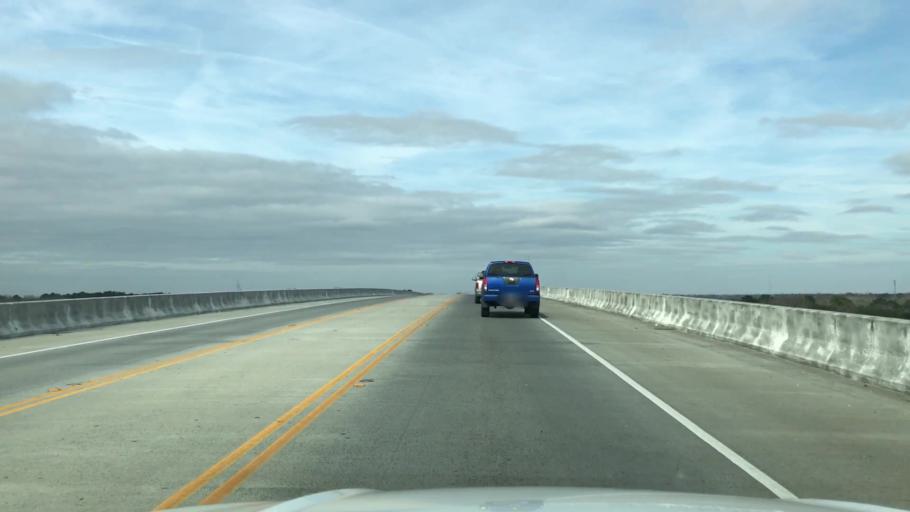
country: US
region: South Carolina
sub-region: Charleston County
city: Shell Point
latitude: 32.7846
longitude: -80.1071
